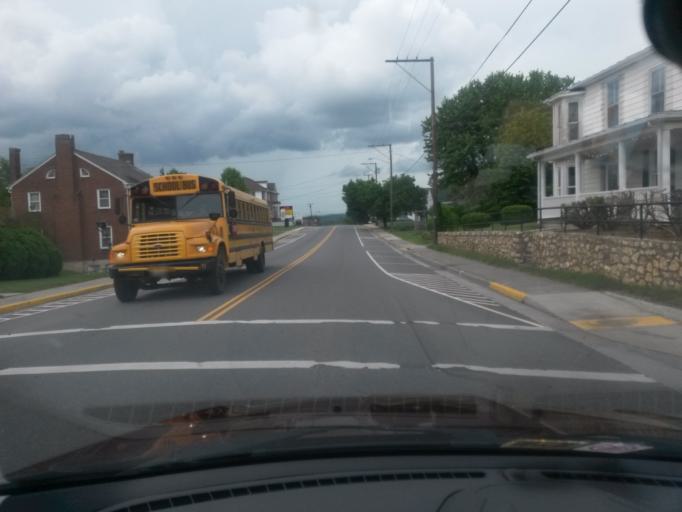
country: US
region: Virginia
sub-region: Floyd County
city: Floyd
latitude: 36.9125
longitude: -80.3205
